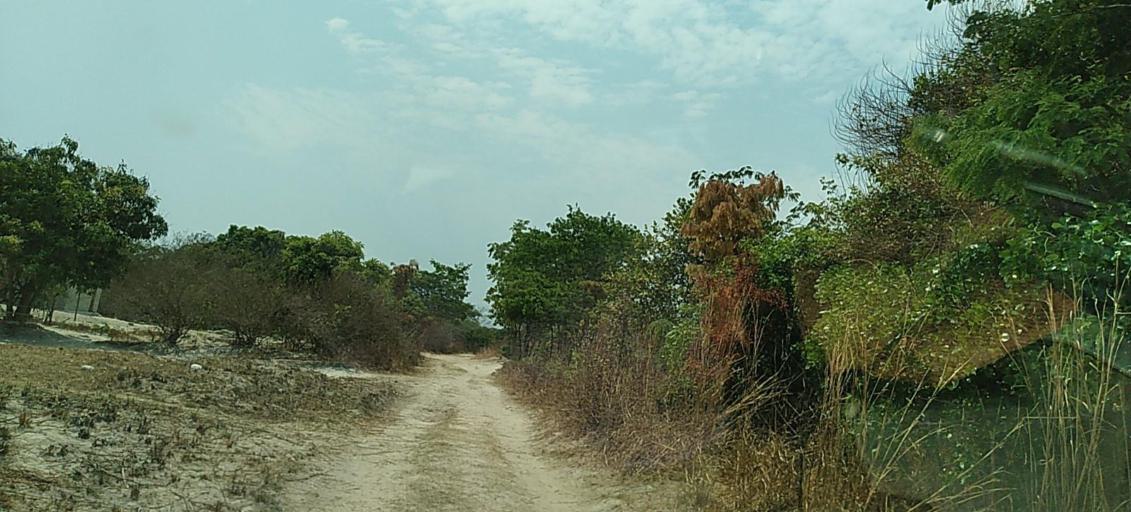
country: ZM
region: Copperbelt
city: Kalulushi
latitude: -12.9512
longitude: 28.1361
